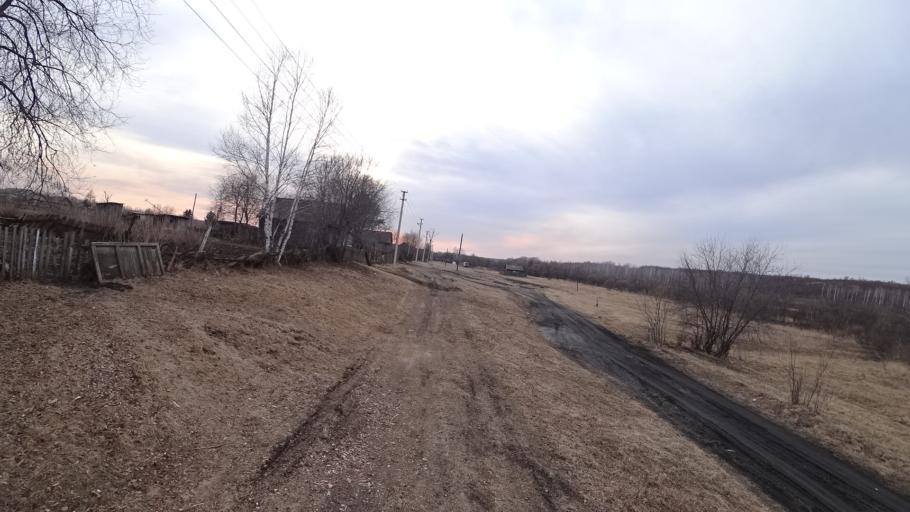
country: RU
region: Amur
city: Bureya
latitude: 50.0216
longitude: 129.7716
